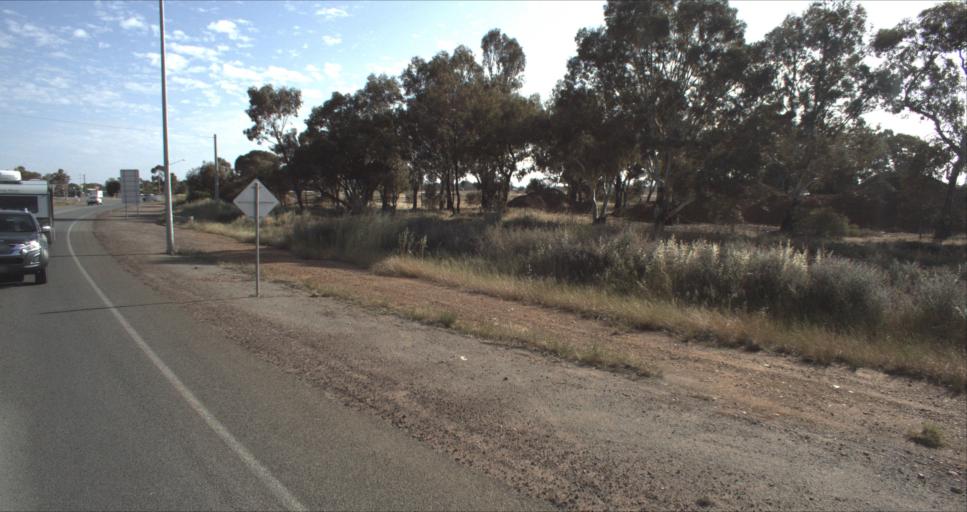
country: AU
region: New South Wales
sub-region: Leeton
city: Leeton
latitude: -34.5709
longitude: 146.3943
